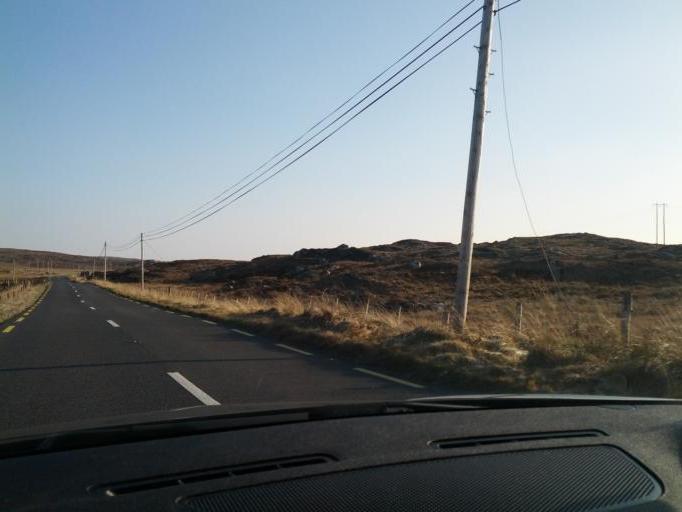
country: IE
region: Connaught
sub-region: County Galway
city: Oughterard
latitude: 53.3552
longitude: -9.5423
